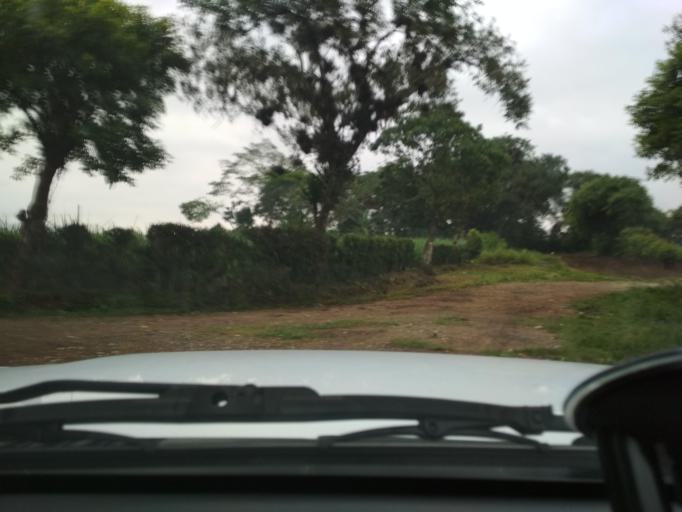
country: MX
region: Veracruz
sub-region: Fortin
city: Monte Salas
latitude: 18.9218
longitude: -97.0412
